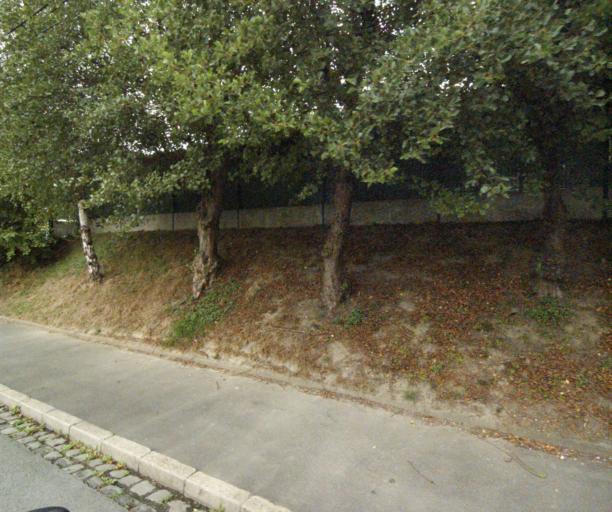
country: FR
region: Nord-Pas-de-Calais
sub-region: Departement du Nord
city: Ronchin
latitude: 50.6085
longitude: 3.0895
